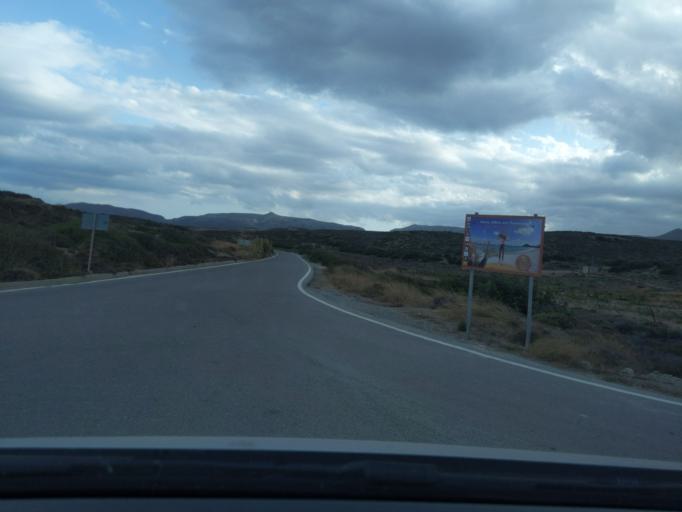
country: GR
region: Crete
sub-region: Nomos Lasithiou
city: Palekastro
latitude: 35.2412
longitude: 26.2480
